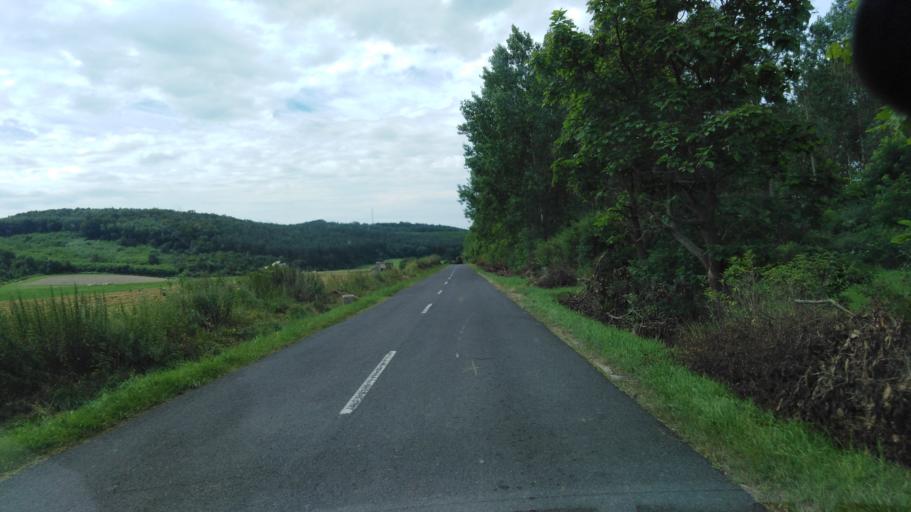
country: HU
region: Nograd
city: Karancskeszi
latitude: 48.2285
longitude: 19.6179
